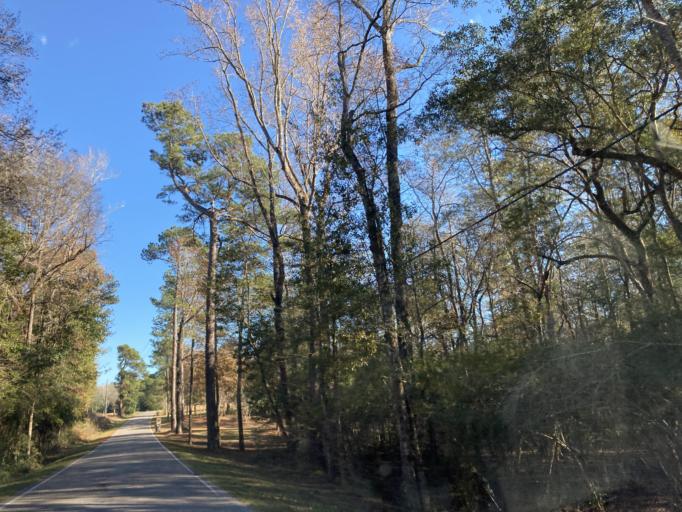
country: US
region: Mississippi
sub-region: Lamar County
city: Sumrall
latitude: 31.3669
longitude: -89.5753
